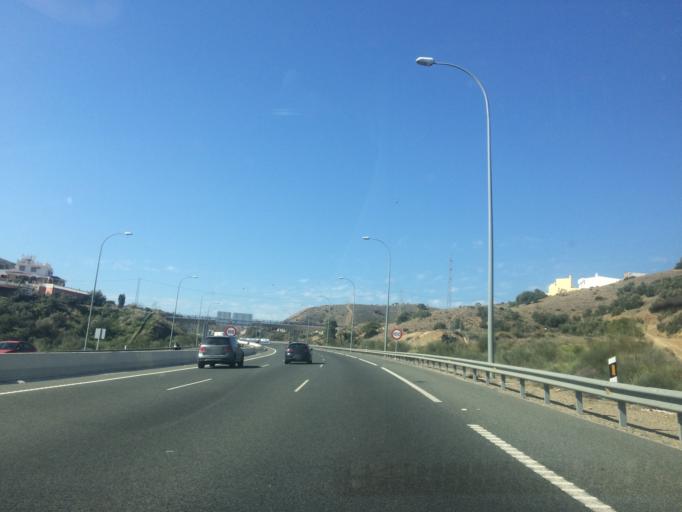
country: ES
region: Andalusia
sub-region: Provincia de Malaga
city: Malaga
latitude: 36.7436
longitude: -4.4496
